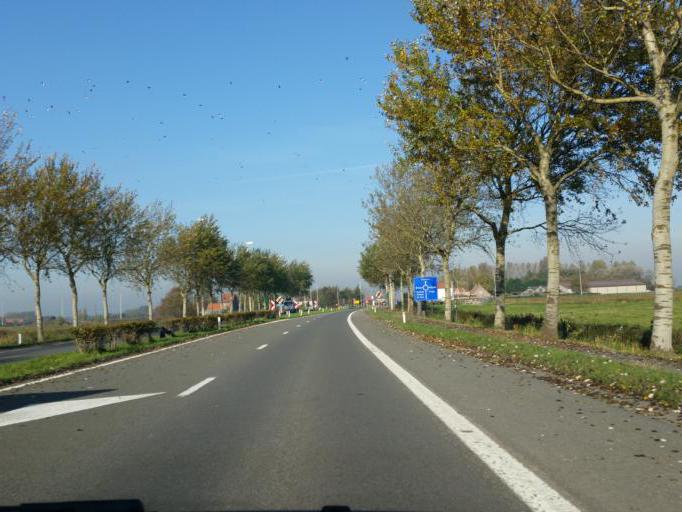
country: BE
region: Flanders
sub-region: Provincie West-Vlaanderen
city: De Haan
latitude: 51.2298
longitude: 3.0617
